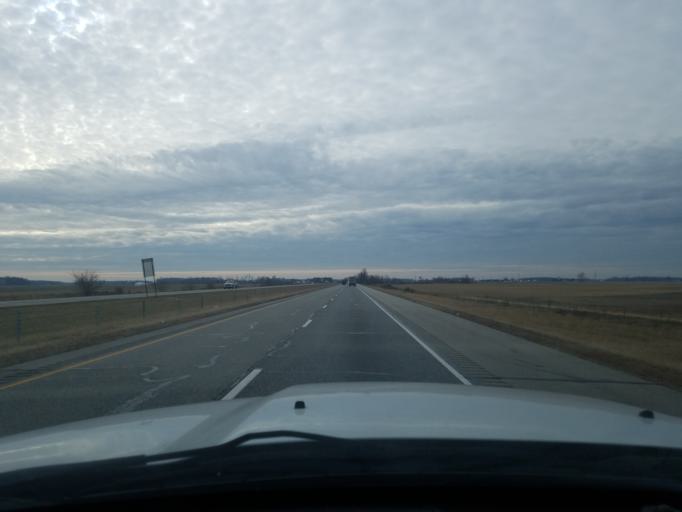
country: US
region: Indiana
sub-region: Huntington County
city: Warren
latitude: 40.6931
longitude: -85.4710
